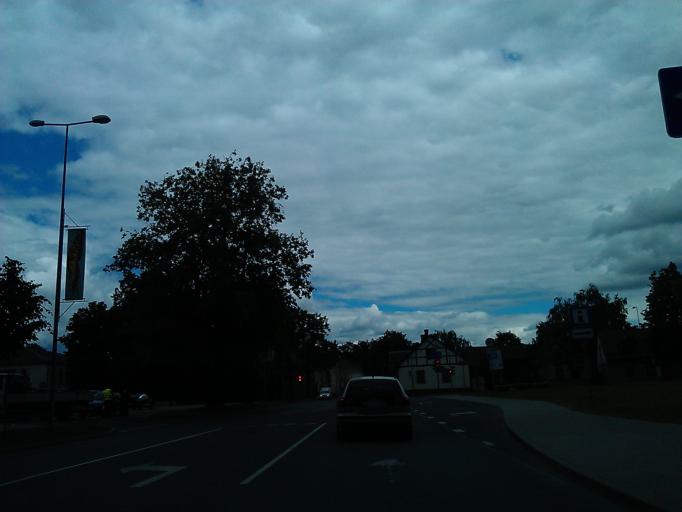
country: LV
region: Dobeles Rajons
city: Dobele
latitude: 56.6254
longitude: 23.2807
